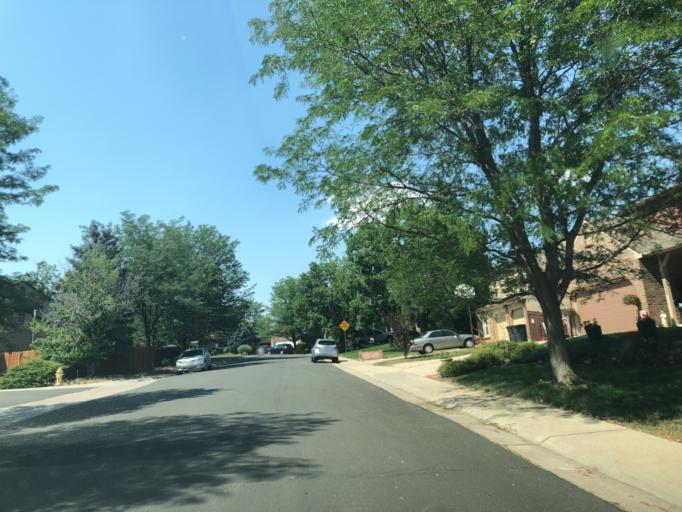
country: US
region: Colorado
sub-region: Arapahoe County
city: Dove Valley
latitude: 39.6346
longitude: -104.7637
